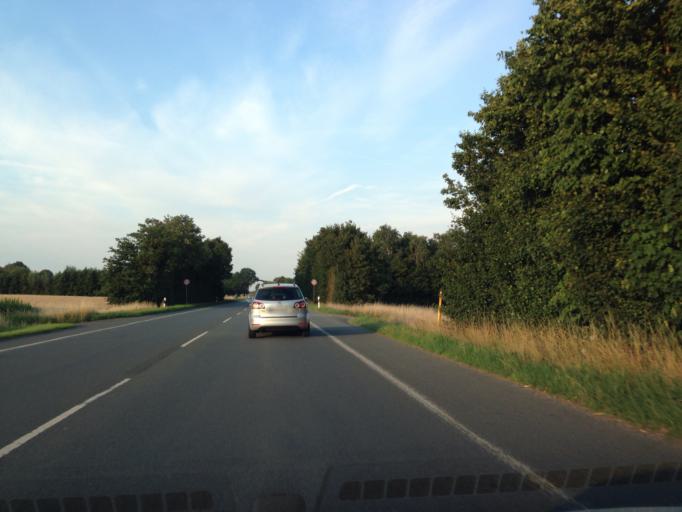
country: DE
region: North Rhine-Westphalia
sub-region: Regierungsbezirk Munster
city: Senden
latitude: 51.8722
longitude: 7.5598
